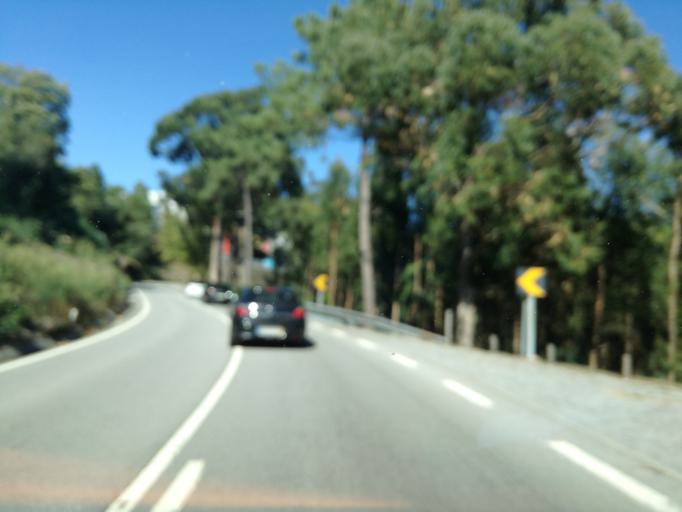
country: PT
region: Porto
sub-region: Pacos de Ferreira
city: Seroa
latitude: 41.2564
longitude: -8.4471
